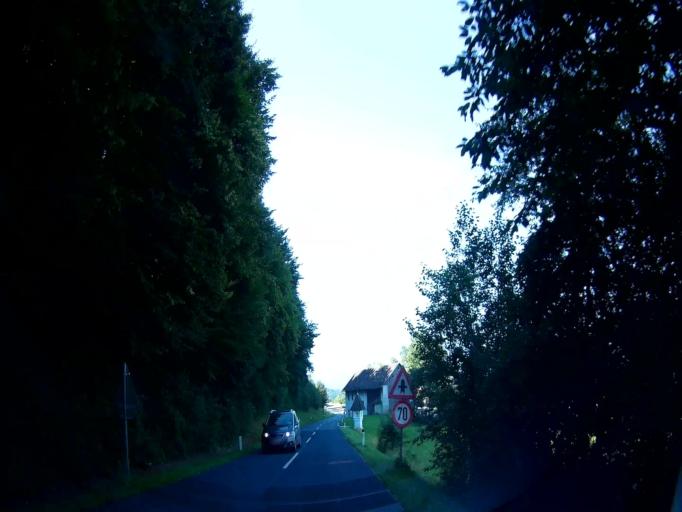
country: AT
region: Carinthia
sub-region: Politischer Bezirk Volkermarkt
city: Gallizien
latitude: 46.6012
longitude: 14.5305
